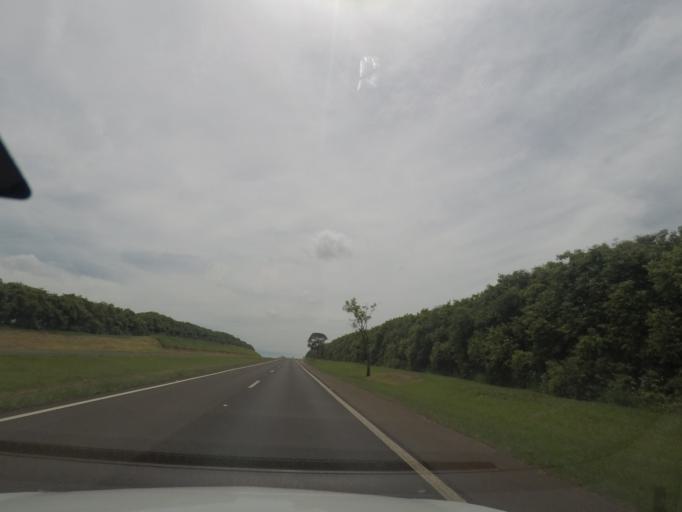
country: BR
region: Sao Paulo
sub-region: Bebedouro
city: Bebedouro
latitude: -21.0143
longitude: -48.4260
